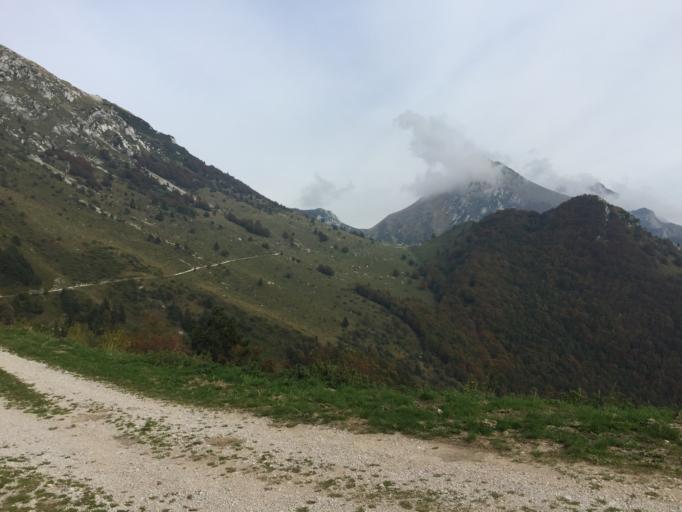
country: IT
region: Friuli Venezia Giulia
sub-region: Provincia di Udine
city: Resiutta
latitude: 46.3426
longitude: 13.2052
